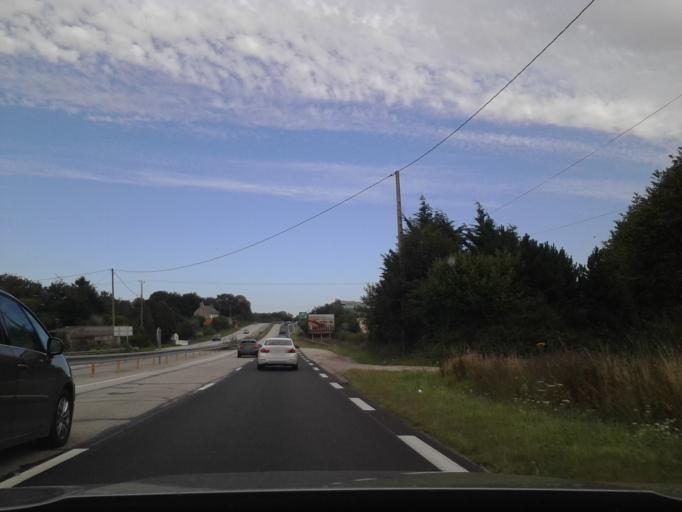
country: FR
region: Lower Normandy
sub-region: Departement de la Manche
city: La Glacerie
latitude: 49.5799
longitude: -1.5855
